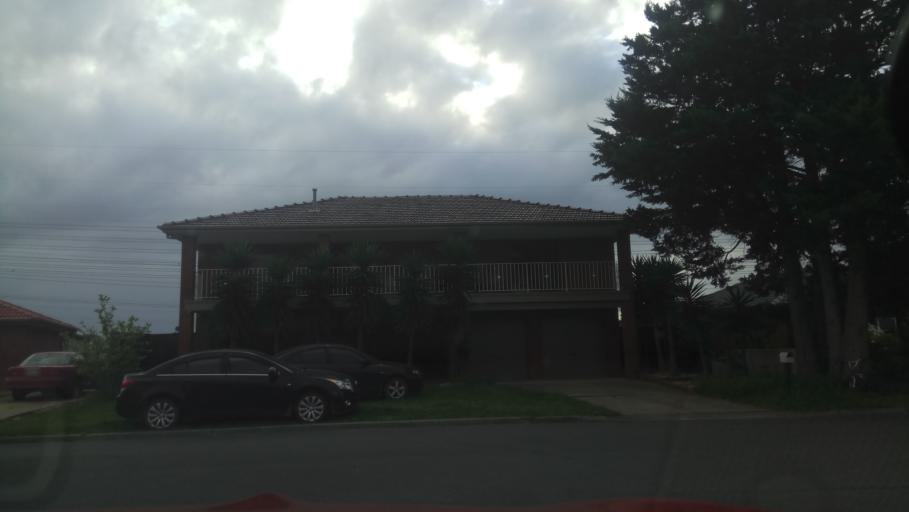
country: AU
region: Victoria
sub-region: Casey
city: Cranbourne North
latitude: -38.0738
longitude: 145.2640
